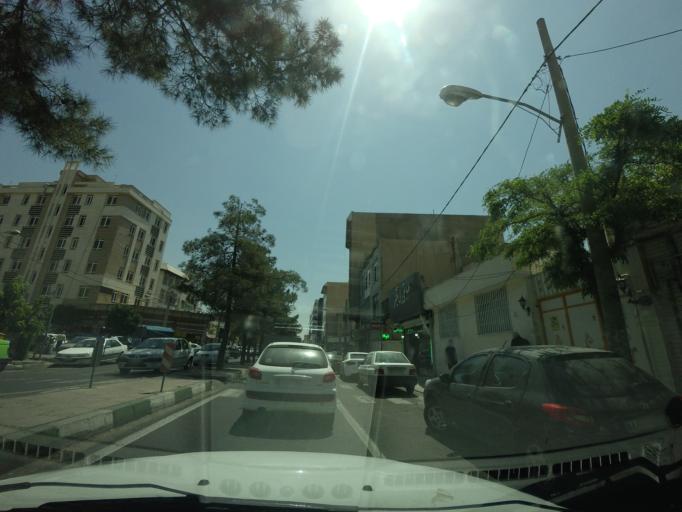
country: IR
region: Tehran
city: Tehran
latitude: 35.7240
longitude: 51.3138
